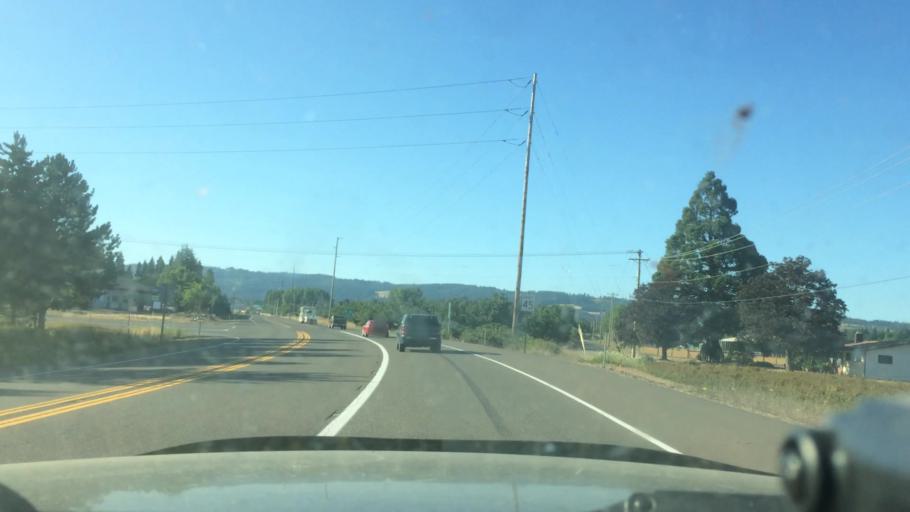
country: US
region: Oregon
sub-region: Yamhill County
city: Newberg
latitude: 45.2854
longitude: -122.9450
